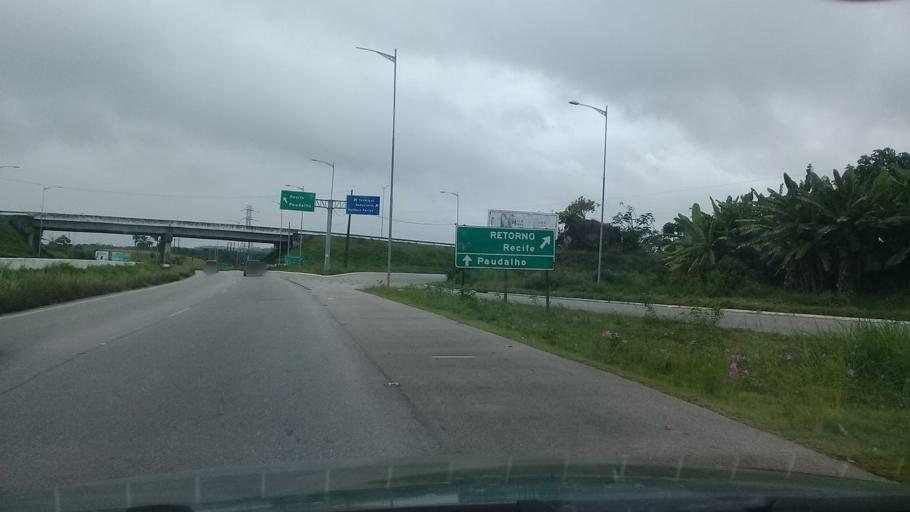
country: BR
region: Pernambuco
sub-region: Jaboatao Dos Guararapes
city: Jaboatao dos Guararapes
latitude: -8.0661
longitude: -34.9901
